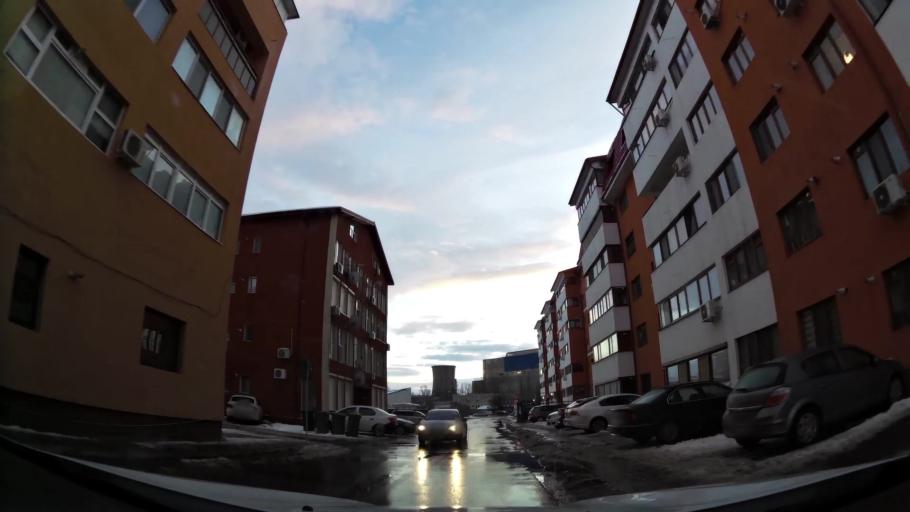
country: RO
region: Ilfov
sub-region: Comuna Popesti-Leordeni
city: Popesti-Leordeni
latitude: 44.3646
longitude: 26.1494
